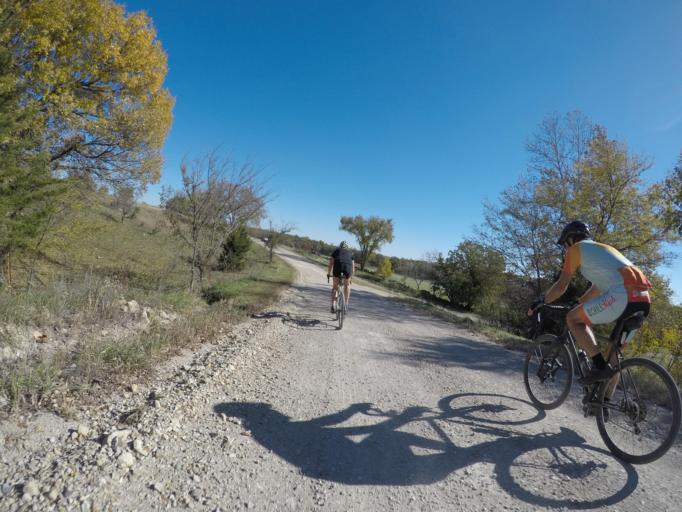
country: US
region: Kansas
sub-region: Wabaunsee County
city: Alma
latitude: 38.9468
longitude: -96.4624
